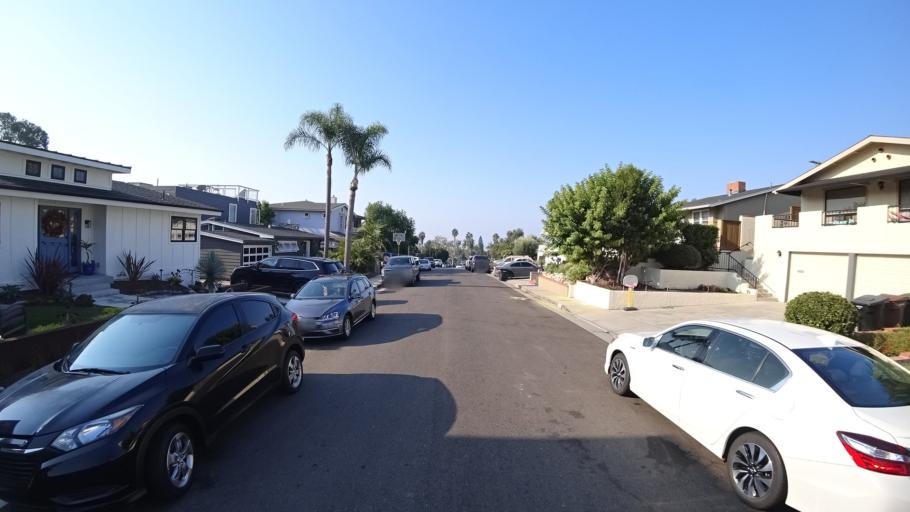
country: US
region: California
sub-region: Orange County
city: San Clemente
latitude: 33.4125
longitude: -117.6042
